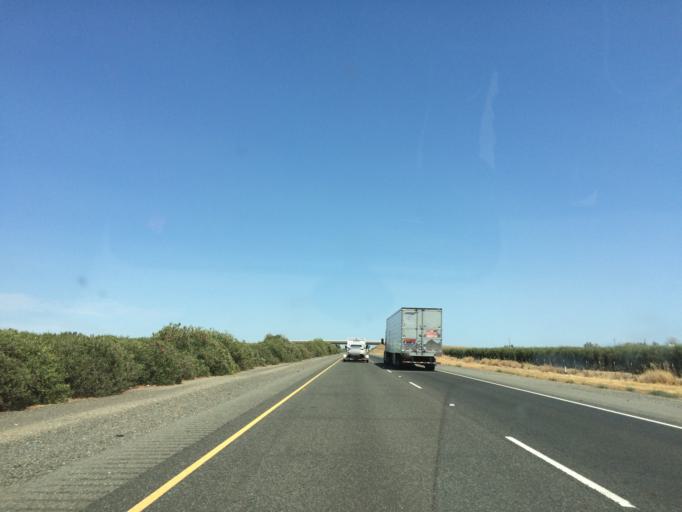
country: US
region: California
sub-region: Glenn County
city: Willows
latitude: 39.6076
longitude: -122.2078
